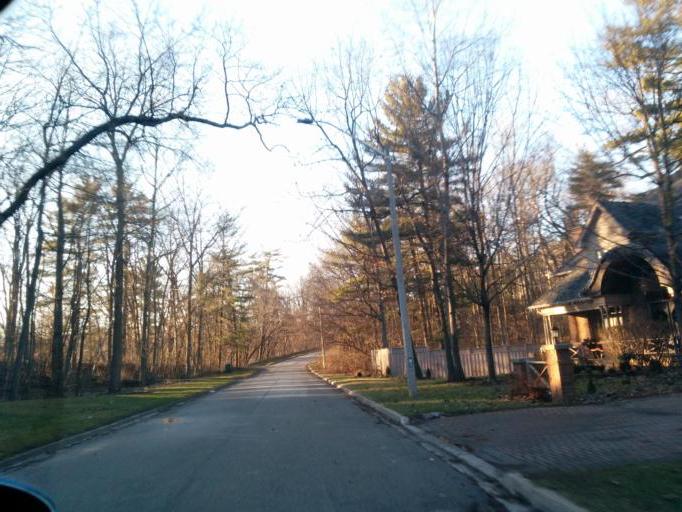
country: CA
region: Ontario
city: Mississauga
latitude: 43.5581
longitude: -79.6129
